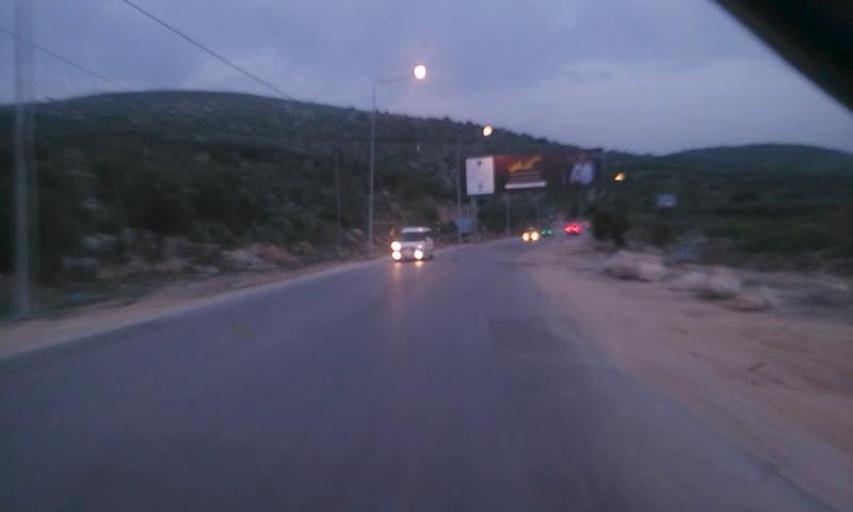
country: PS
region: West Bank
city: `Anabta
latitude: 32.3020
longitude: 35.1311
